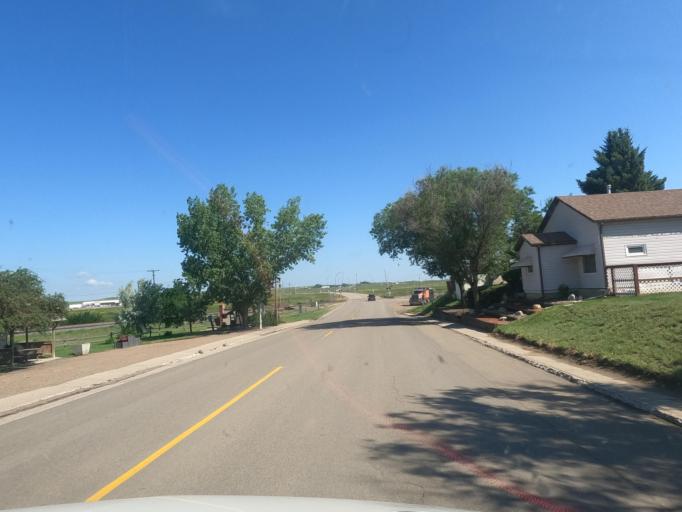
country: CA
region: Saskatchewan
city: Shaunavon
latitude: 50.0983
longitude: -108.4832
